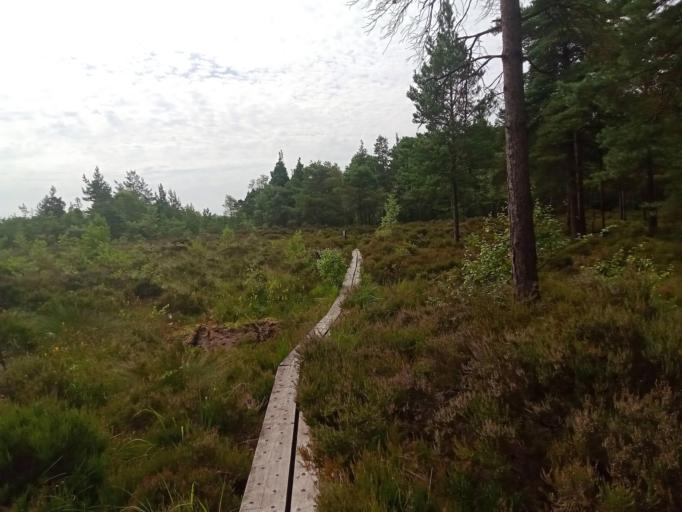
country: IE
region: Leinster
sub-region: Laois
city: Abbeyleix
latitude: 52.8873
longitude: -7.3591
